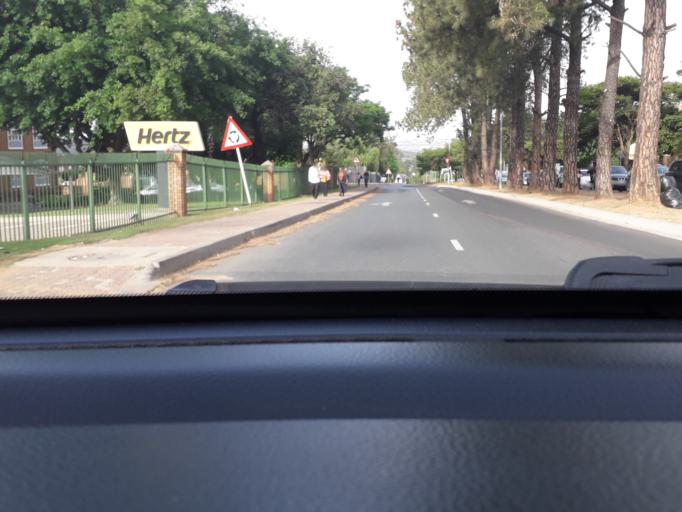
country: ZA
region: Gauteng
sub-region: City of Johannesburg Metropolitan Municipality
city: Diepsloot
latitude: -26.0419
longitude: 28.0167
